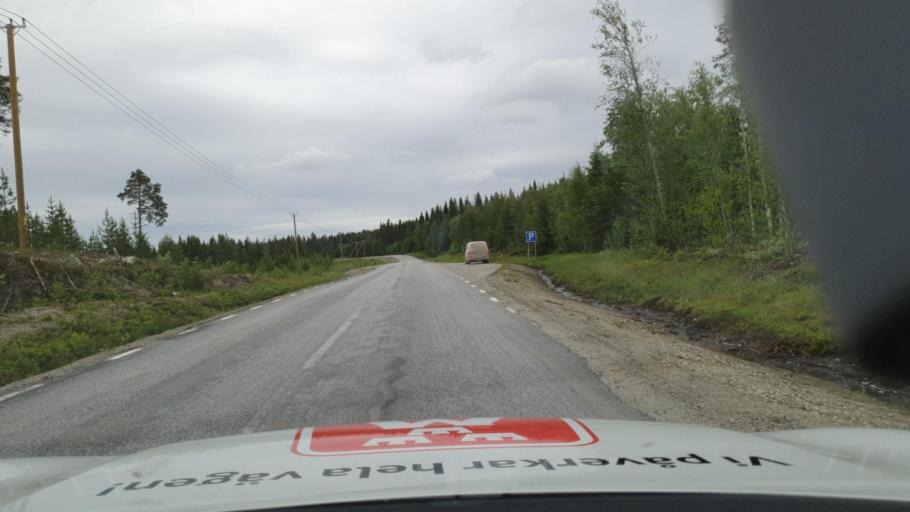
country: SE
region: Vaesterbotten
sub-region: Lycksele Kommun
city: Lycksele
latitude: 64.1426
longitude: 18.3610
